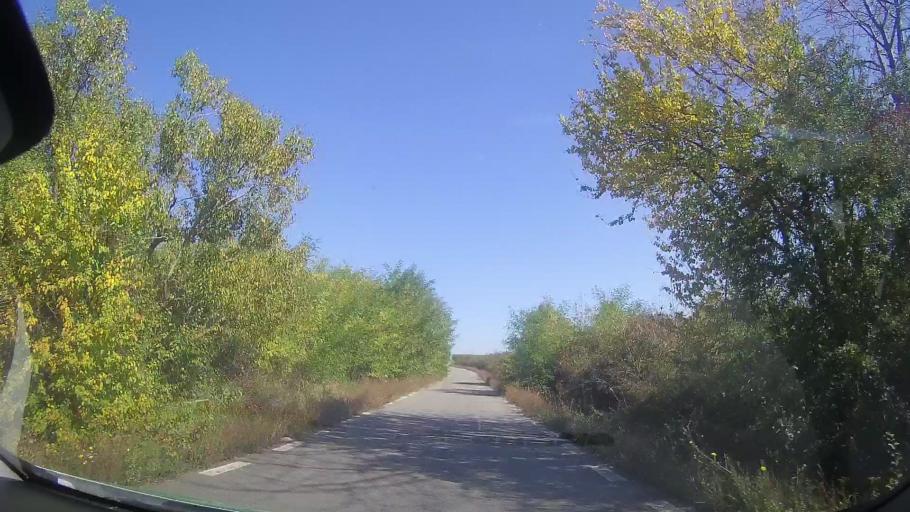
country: RO
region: Timis
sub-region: Comuna Ohaba Lunga
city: Ohaba Lunga
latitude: 45.9161
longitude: 21.9537
